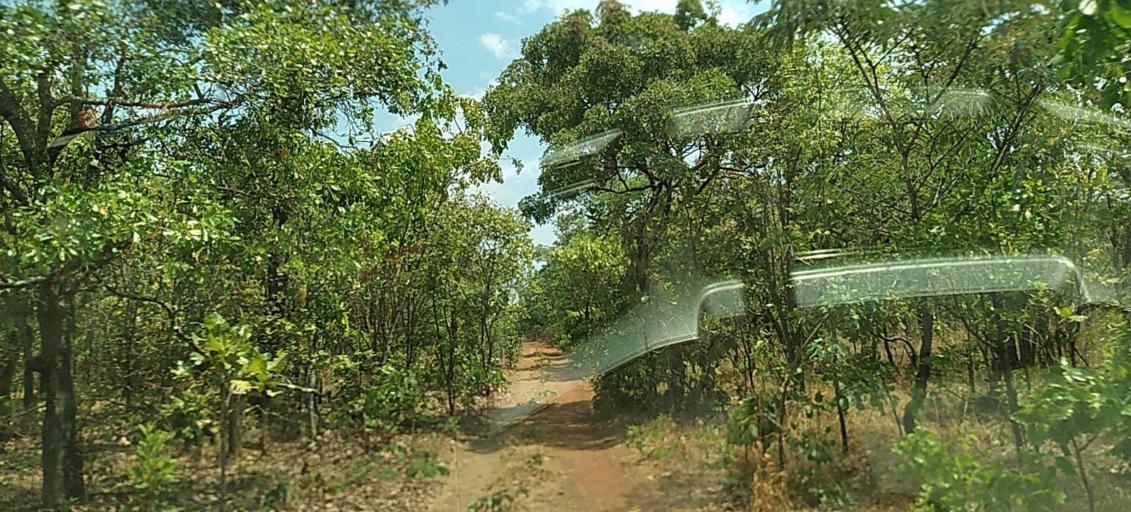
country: CD
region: Katanga
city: Kipushi
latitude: -11.9819
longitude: 27.4157
